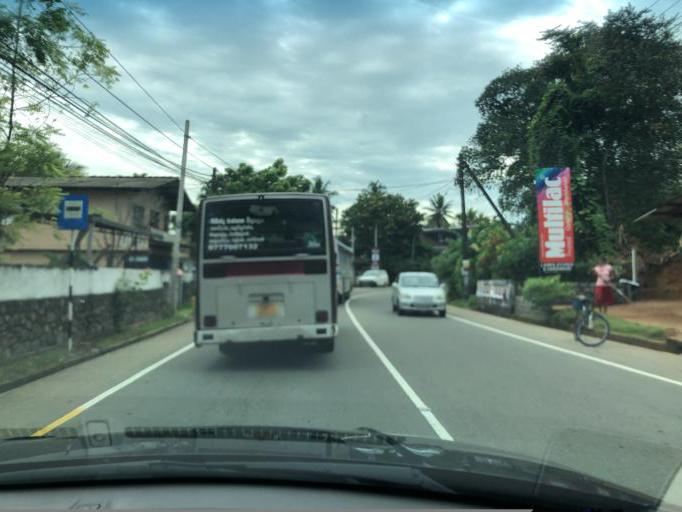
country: LK
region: Western
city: Beruwala
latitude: 6.5427
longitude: 80.0391
